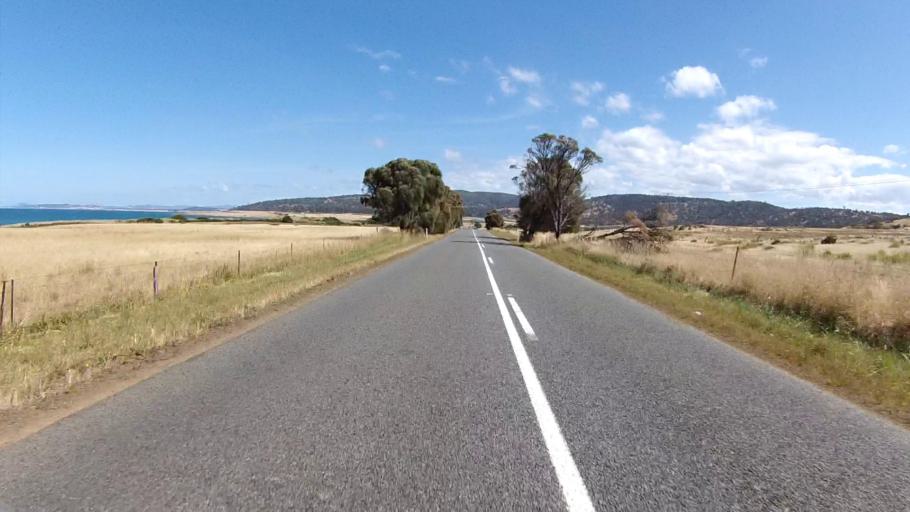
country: AU
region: Tasmania
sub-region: Sorell
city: Sorell
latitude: -42.1944
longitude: 148.0565
